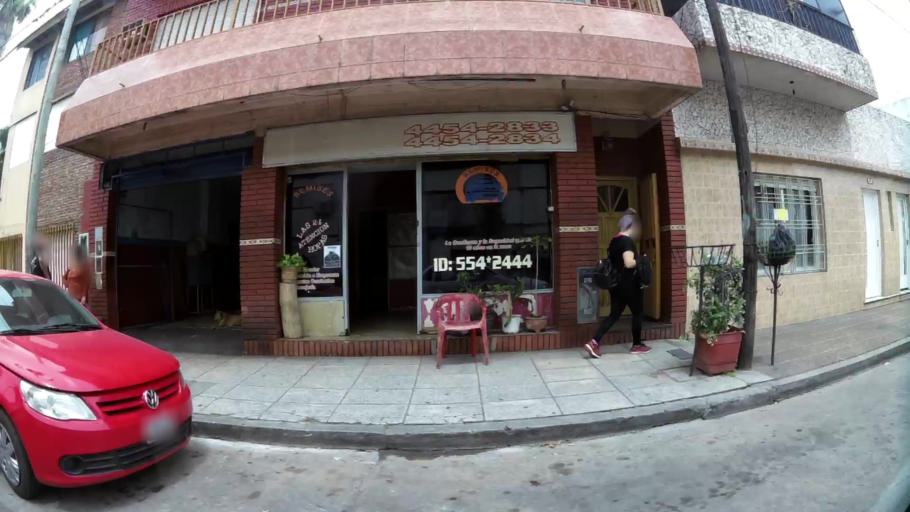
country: AR
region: Buenos Aires
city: San Justo
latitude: -34.6663
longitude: -58.5234
